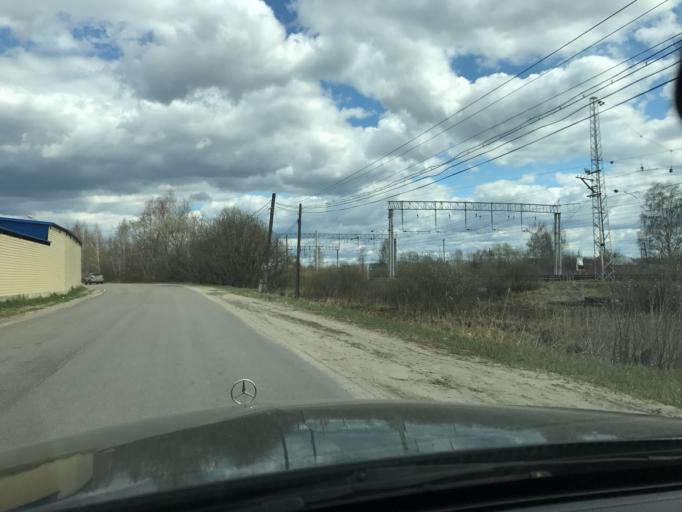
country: RU
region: Vladimir
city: Pokrov
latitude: 55.8893
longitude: 39.2076
